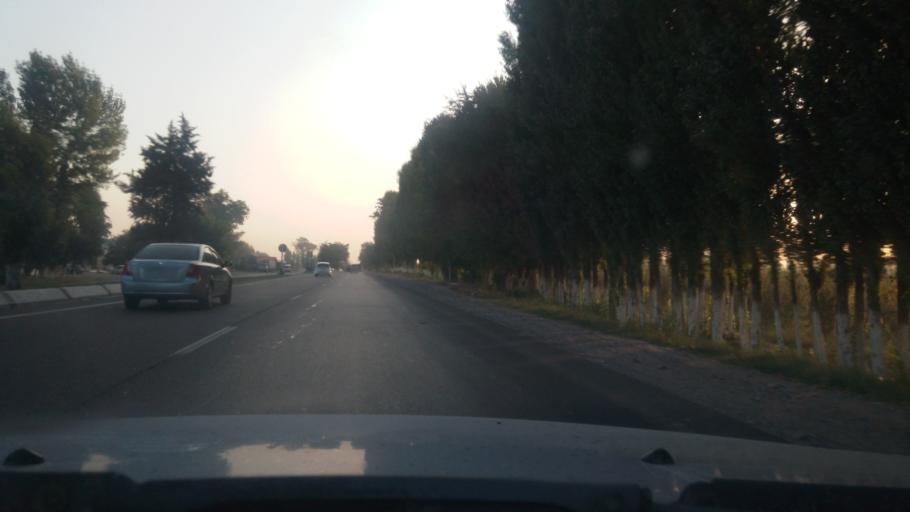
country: UZ
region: Toshkent
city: Yangiyul
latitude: 41.1719
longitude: 69.0671
